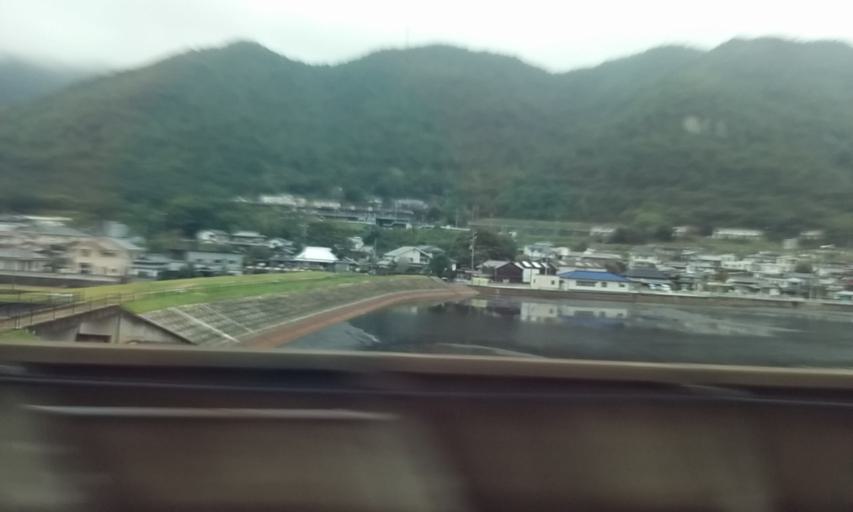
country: JP
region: Okayama
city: Okayama-shi
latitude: 34.7356
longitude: 134.1408
